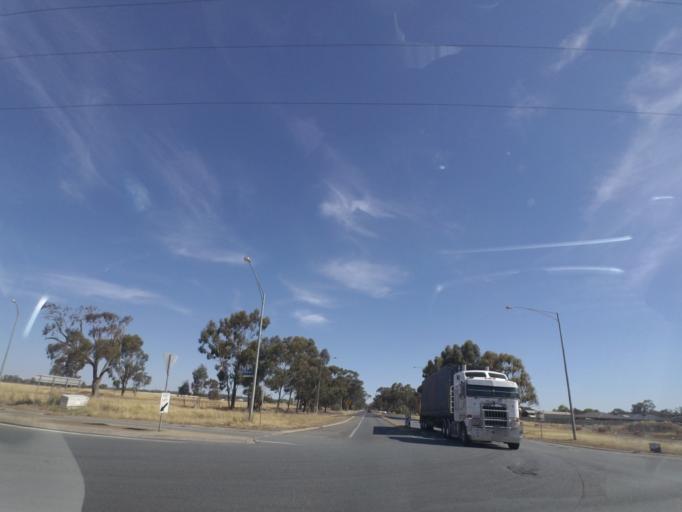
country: AU
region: Victoria
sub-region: Greater Shepparton
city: Shepparton
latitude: -36.4406
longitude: 145.3889
